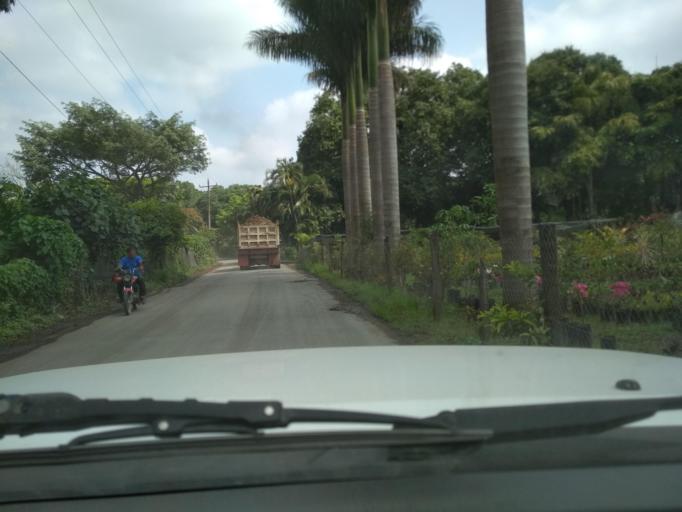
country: MX
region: Veracruz
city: El Tejar
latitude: 19.0795
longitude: -96.1725
